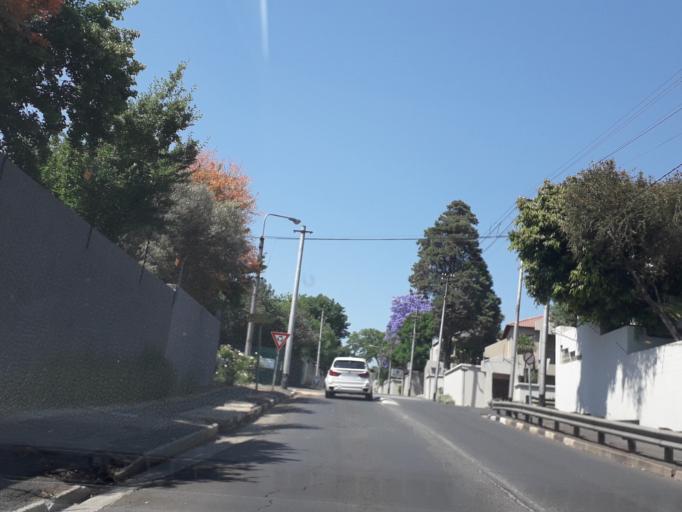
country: ZA
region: Gauteng
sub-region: City of Johannesburg Metropolitan Municipality
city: Johannesburg
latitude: -26.1410
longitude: 28.0234
